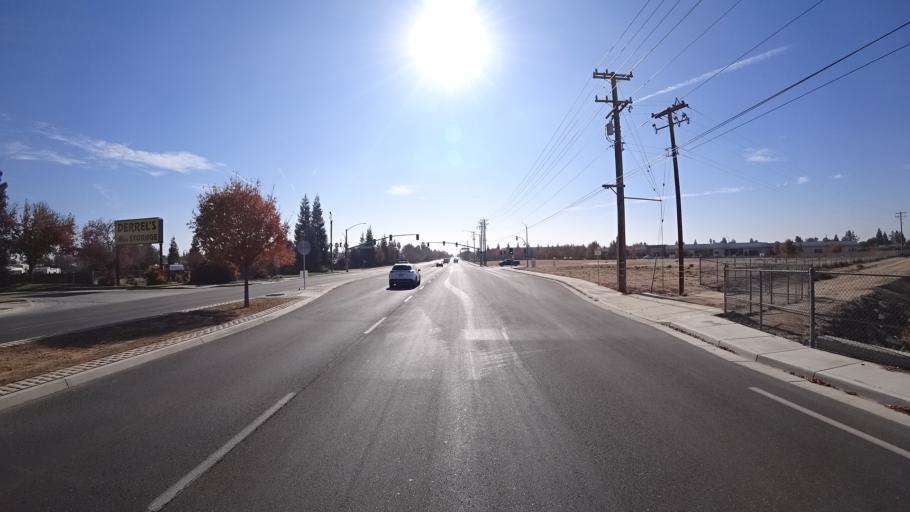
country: US
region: California
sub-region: Kern County
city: Greenacres
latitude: 35.3094
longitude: -119.0745
